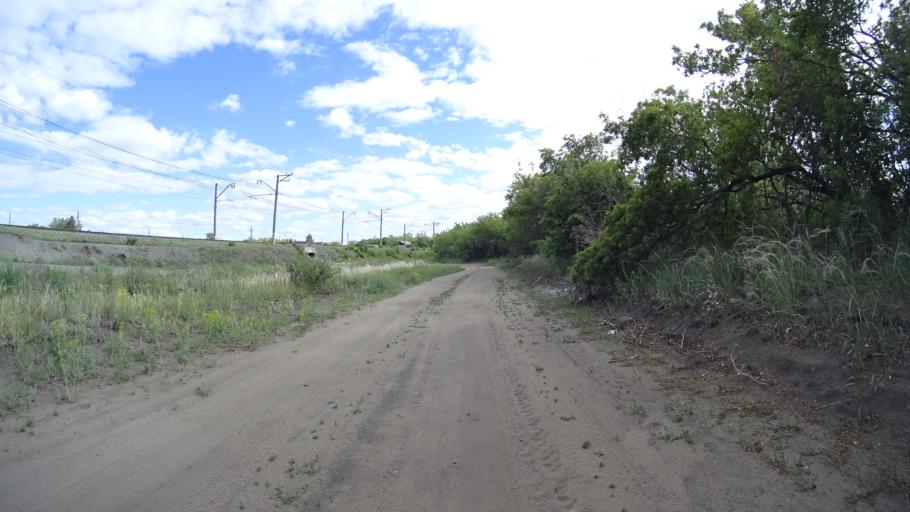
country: RU
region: Chelyabinsk
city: Troitsk
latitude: 54.0702
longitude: 61.6246
